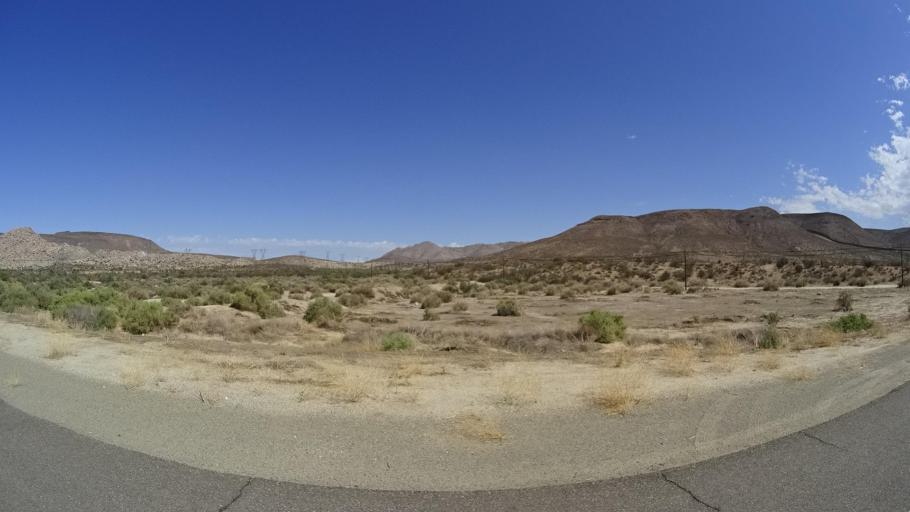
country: MX
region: Baja California
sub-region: Tecate
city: Cereso del Hongo
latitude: 32.6242
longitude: -116.1593
